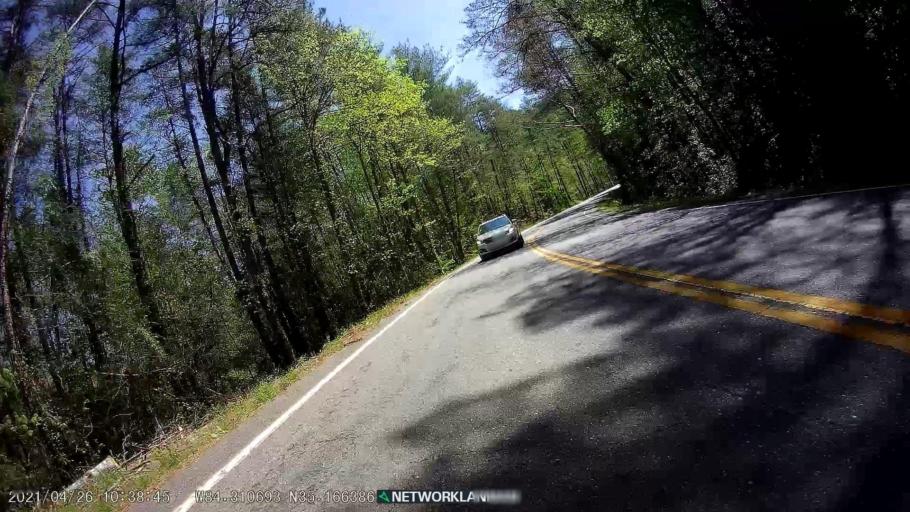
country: US
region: Georgia
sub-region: Fannin County
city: McCaysville
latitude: 35.1666
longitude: -84.3108
